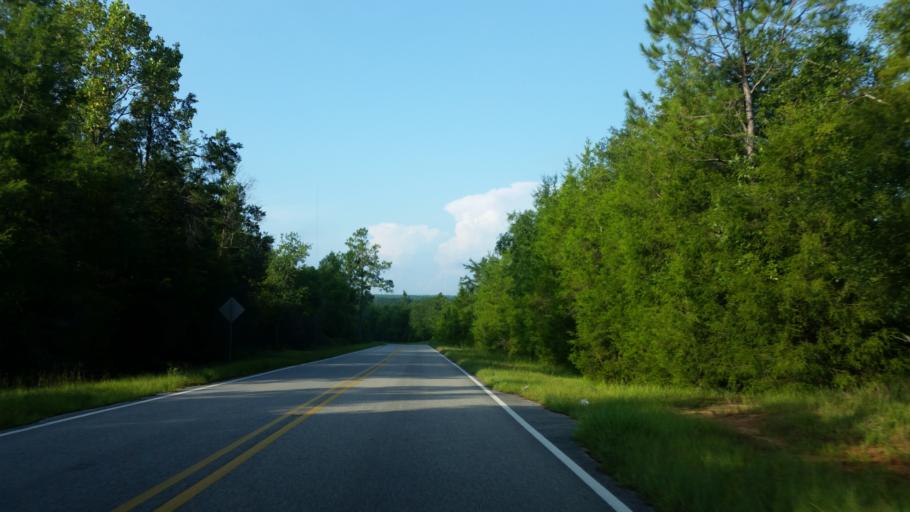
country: US
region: Alabama
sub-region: Baldwin County
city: Robertsdale
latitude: 30.6123
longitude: -87.5442
